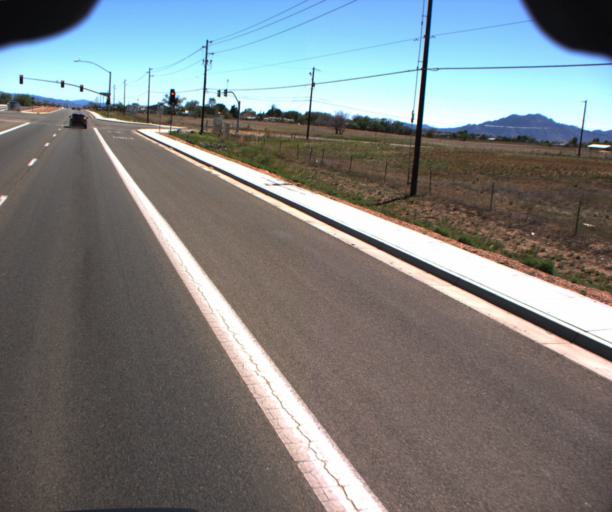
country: US
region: Arizona
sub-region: Yavapai County
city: Chino Valley
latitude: 34.7392
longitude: -112.4546
